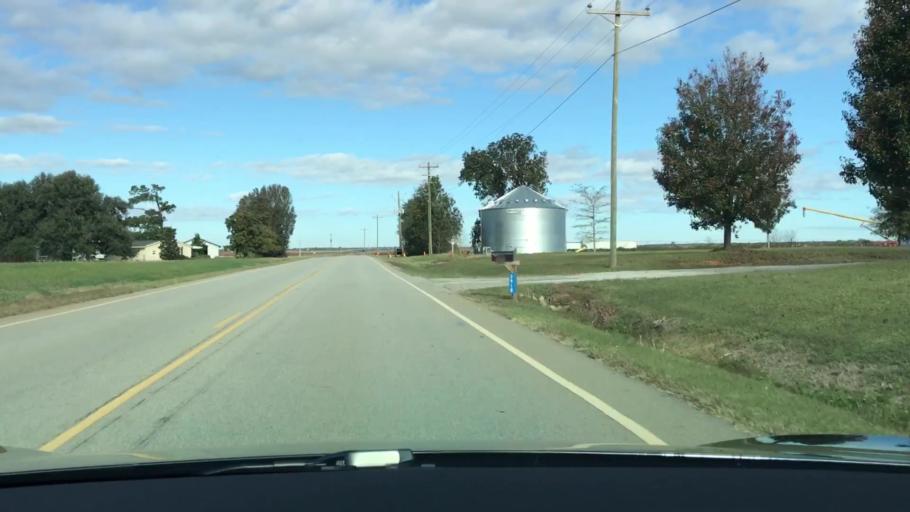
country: US
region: Georgia
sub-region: Jefferson County
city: Wrens
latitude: 33.1071
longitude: -82.4259
